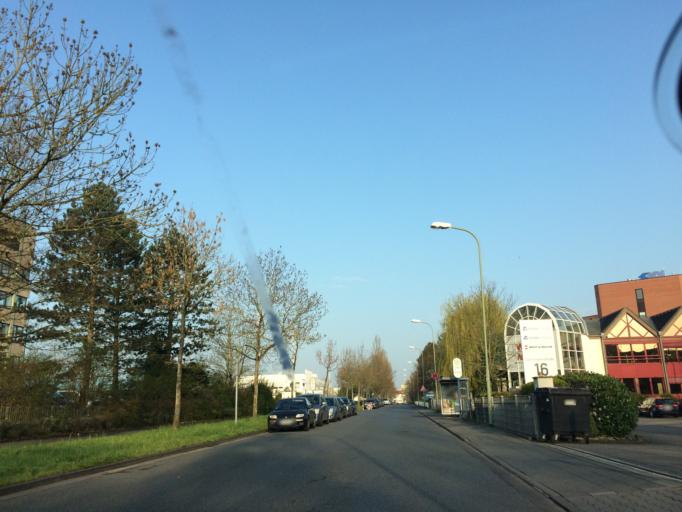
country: DE
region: Hesse
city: Obertshausen
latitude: 50.0839
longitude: 8.8372
